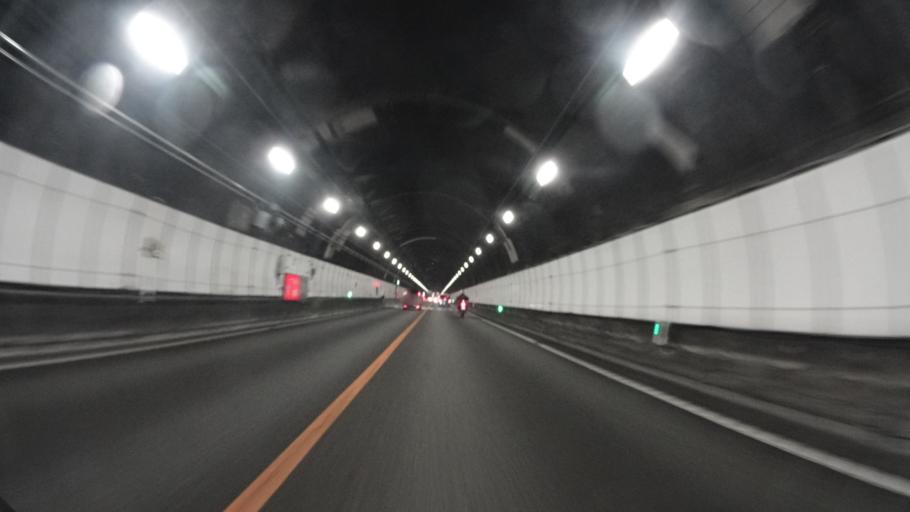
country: JP
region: Shizuoka
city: Gotemba
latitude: 35.3697
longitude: 139.0484
